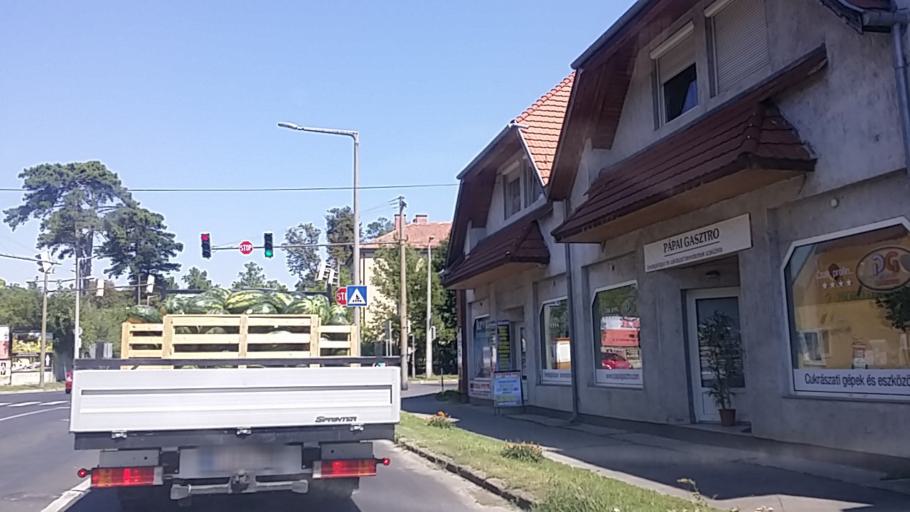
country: HU
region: Zala
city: Keszthely
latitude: 46.7675
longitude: 17.2370
